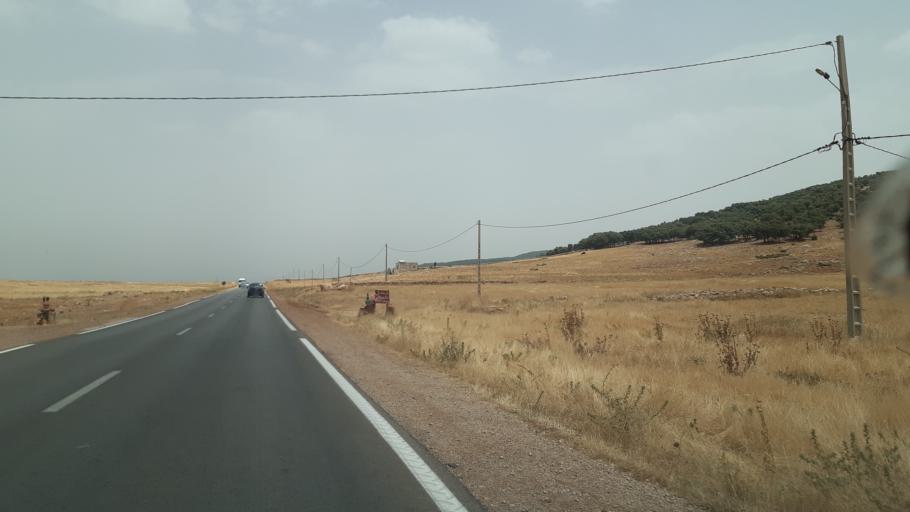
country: MA
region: Meknes-Tafilalet
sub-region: Ifrane
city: Ifrane
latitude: 33.6268
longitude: -5.0782
